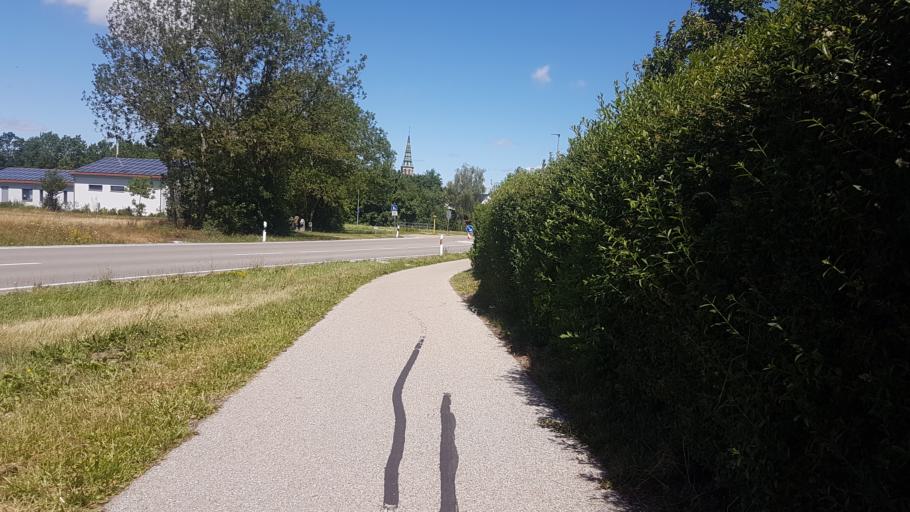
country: DE
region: Bavaria
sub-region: Regierungsbezirk Mittelfranken
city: Aurach
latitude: 49.2585
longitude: 10.4610
